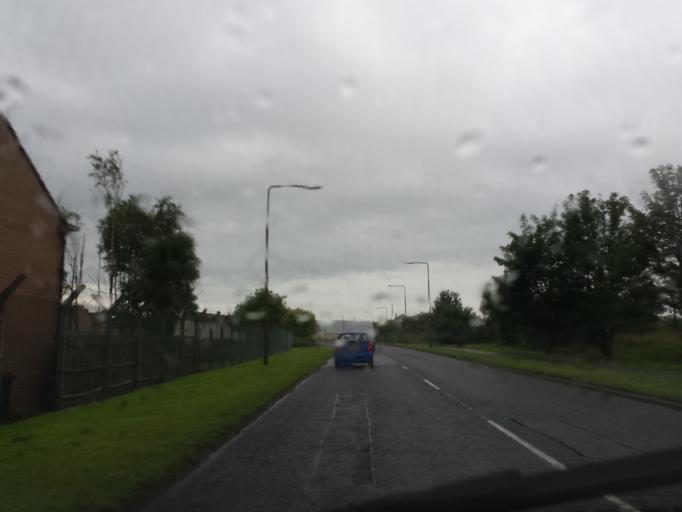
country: GB
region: Scotland
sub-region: Fife
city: Leuchars
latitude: 56.3787
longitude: -2.8900
